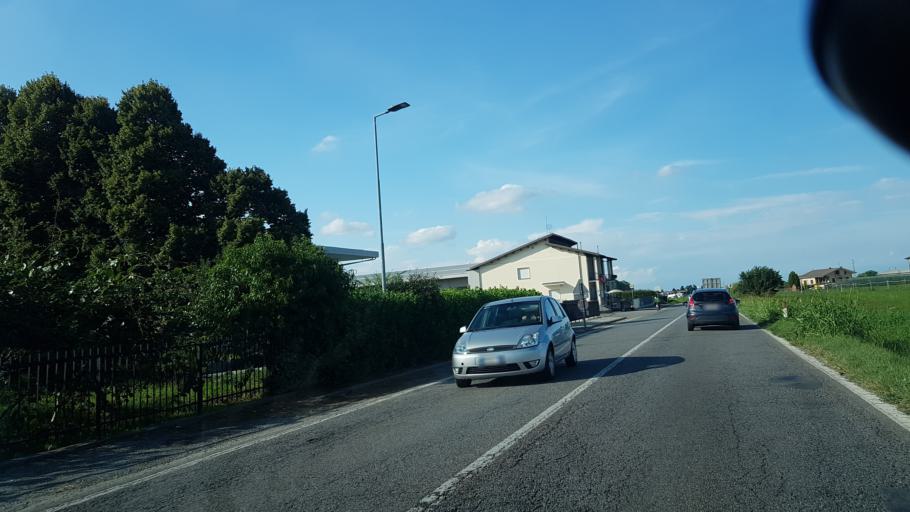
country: IT
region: Piedmont
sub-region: Provincia di Cuneo
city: Busca
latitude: 44.5326
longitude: 7.4841
